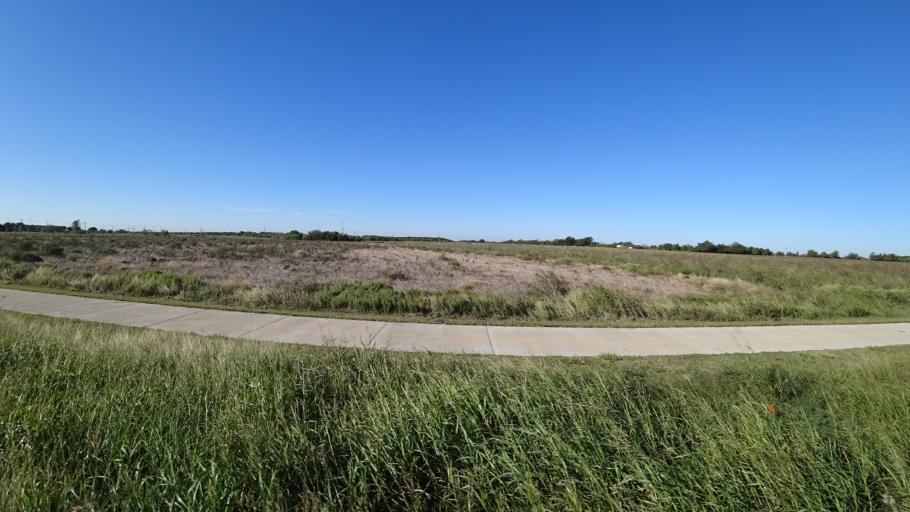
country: US
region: Texas
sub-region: Travis County
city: Manor
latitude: 30.3247
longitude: -97.6319
